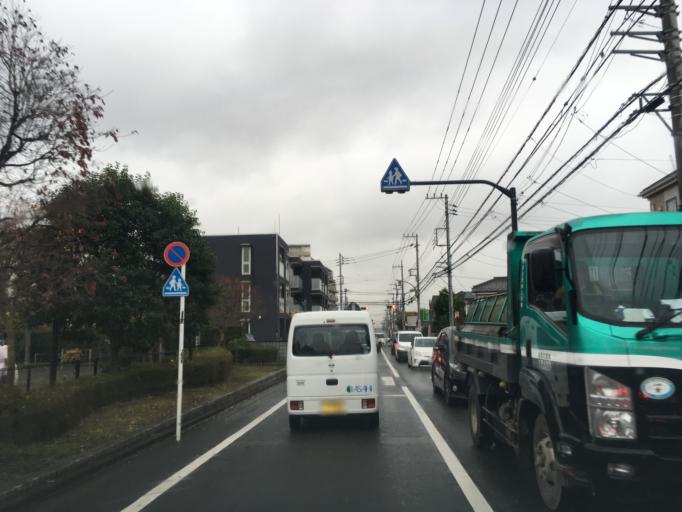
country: JP
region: Tokyo
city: Kokubunji
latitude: 35.7162
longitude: 139.4306
